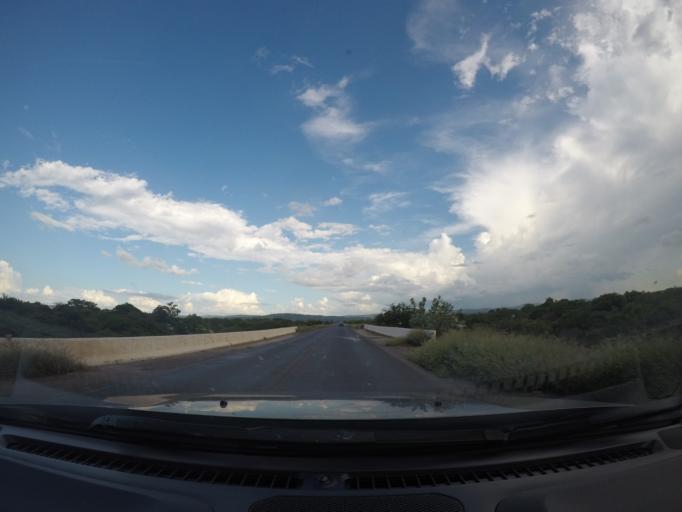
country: BR
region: Bahia
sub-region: Ibotirama
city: Ibotirama
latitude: -12.1771
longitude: -43.2477
